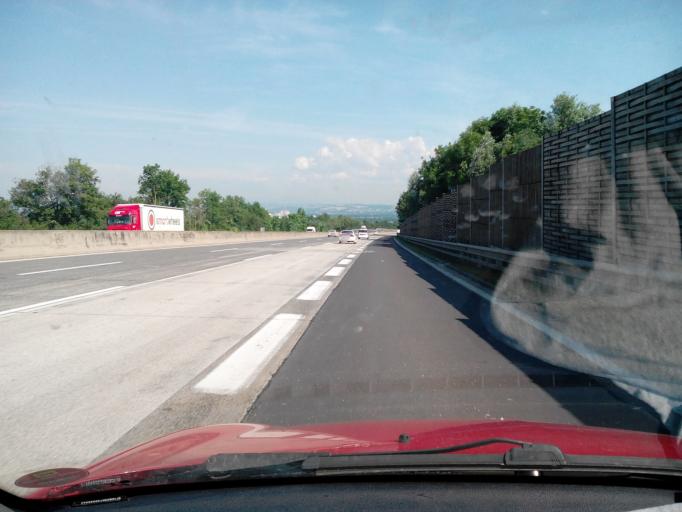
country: AT
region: Lower Austria
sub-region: Politischer Bezirk Amstetten
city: Sankt Valentin
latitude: 48.1657
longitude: 14.5517
